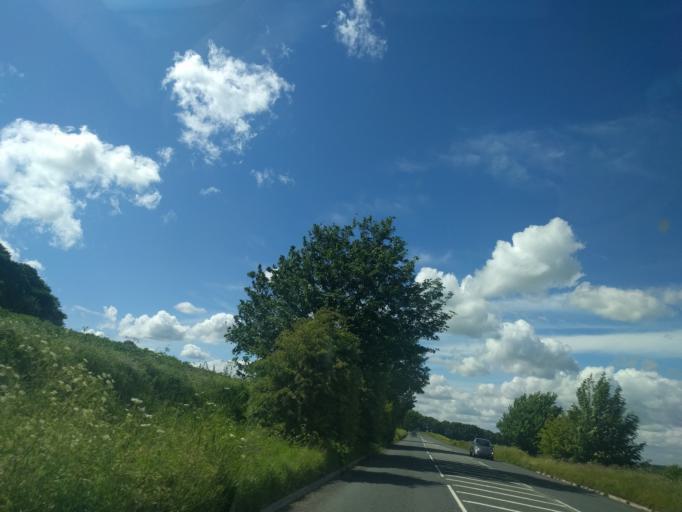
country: GB
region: England
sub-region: Wiltshire
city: Avebury
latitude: 51.4228
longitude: -1.8922
